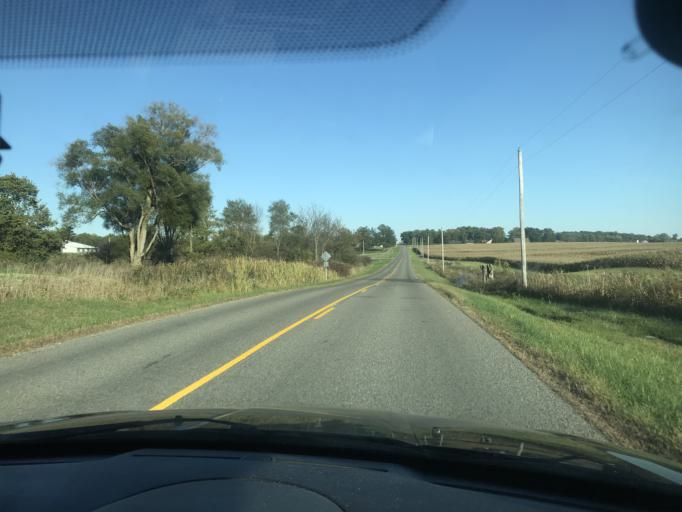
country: US
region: Ohio
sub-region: Logan County
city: De Graff
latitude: 40.3240
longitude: -83.8717
